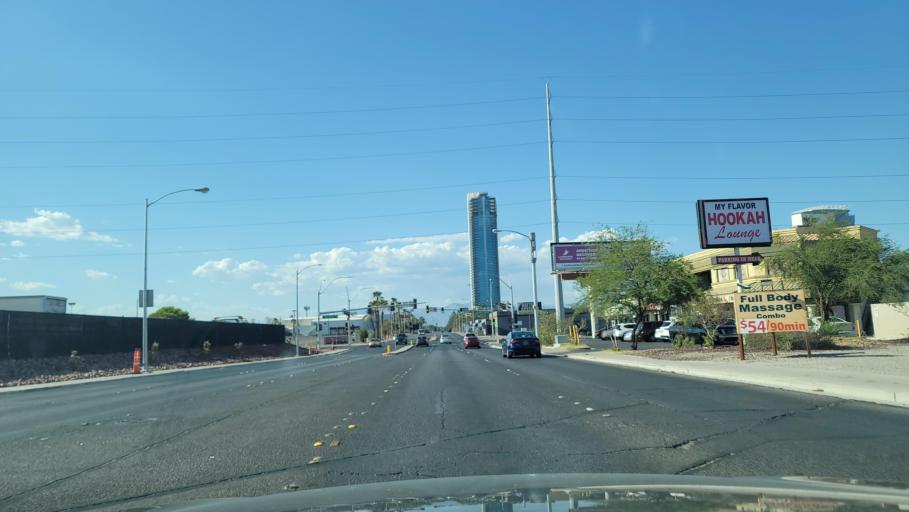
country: US
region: Nevada
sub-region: Clark County
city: Spring Valley
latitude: 36.1071
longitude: -115.1993
